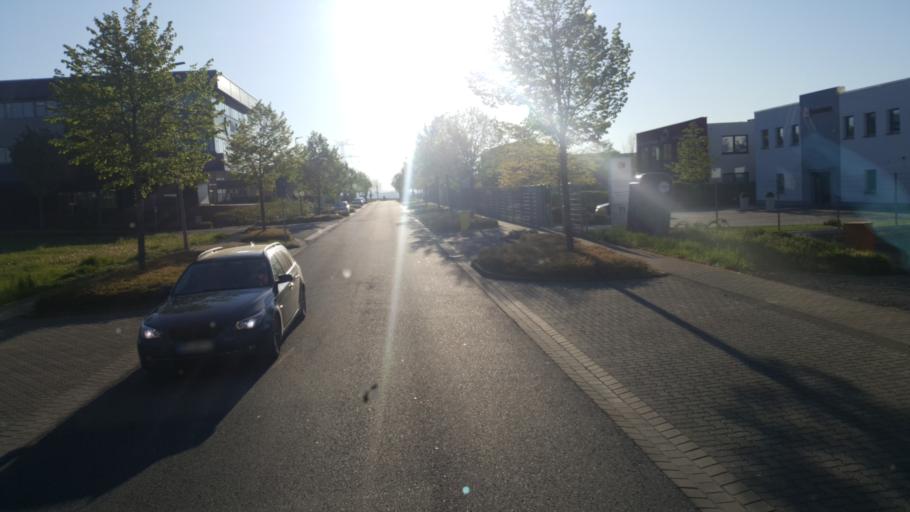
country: DE
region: Rheinland-Pfalz
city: Bad Neuenahr-Ahrweiler
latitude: 50.5800
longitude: 7.0981
